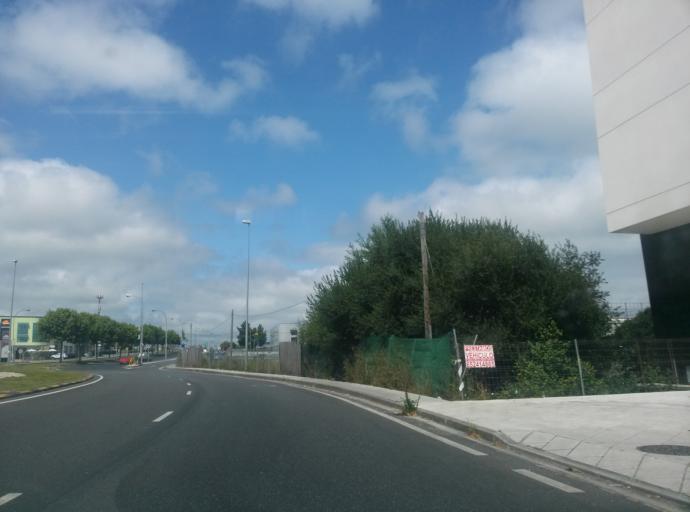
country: ES
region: Galicia
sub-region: Provincia de Lugo
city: Lugo
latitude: 43.0435
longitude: -7.5696
